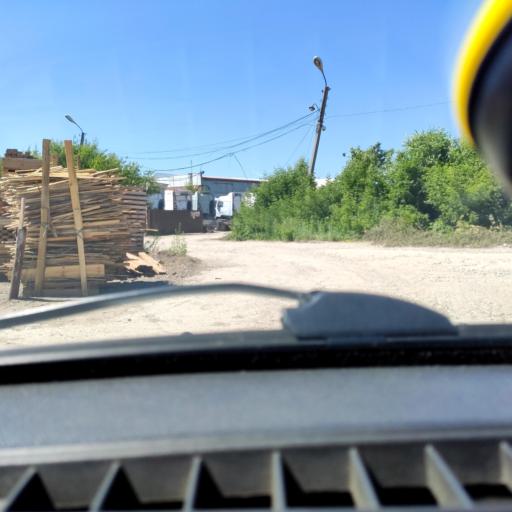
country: RU
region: Samara
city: Tol'yatti
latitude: 53.5693
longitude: 49.2989
